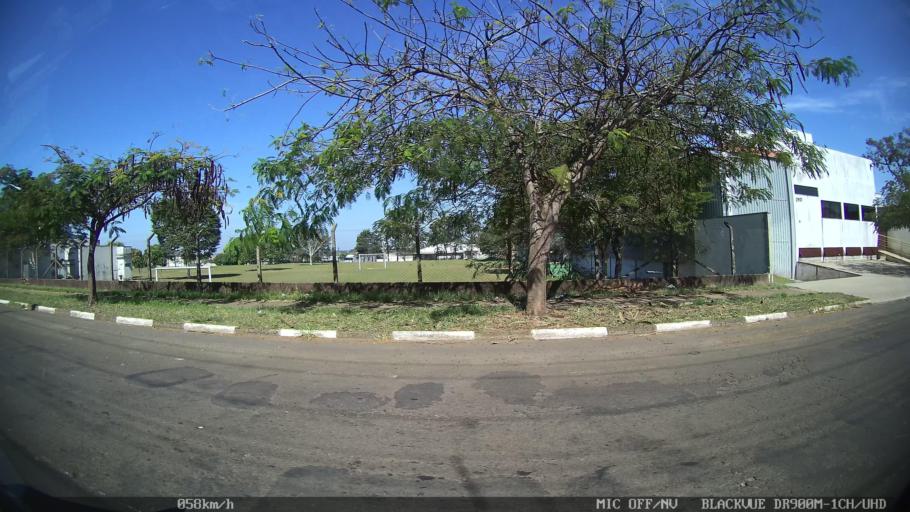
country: BR
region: Sao Paulo
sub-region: Franca
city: Franca
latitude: -20.5530
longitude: -47.4396
